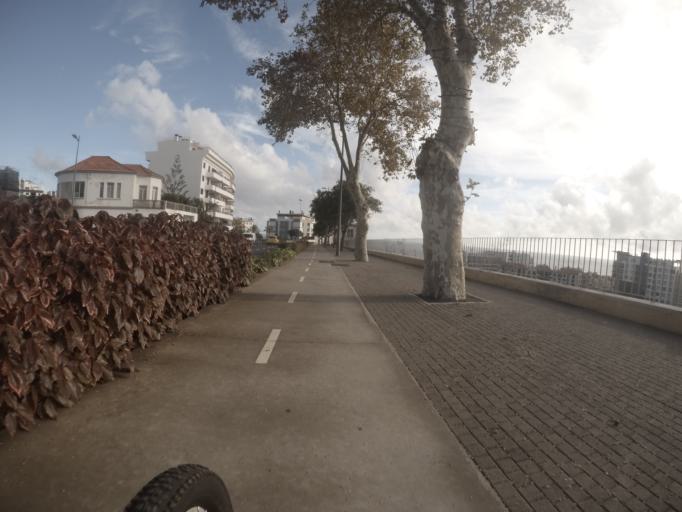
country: PT
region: Madeira
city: Camara de Lobos
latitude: 32.6365
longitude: -16.9447
